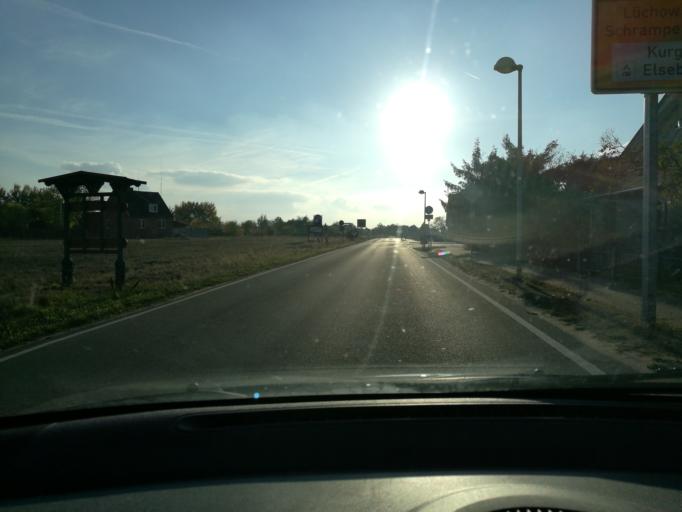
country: DE
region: Saxony-Anhalt
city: Luftkurort Arendsee
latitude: 52.8753
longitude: 11.4643
